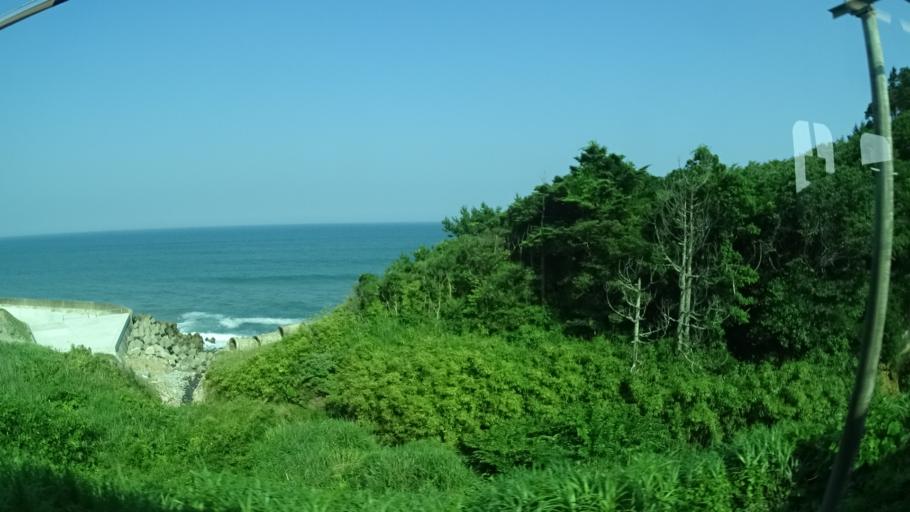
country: JP
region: Fukushima
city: Iwaki
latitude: 37.1908
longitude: 141.0006
